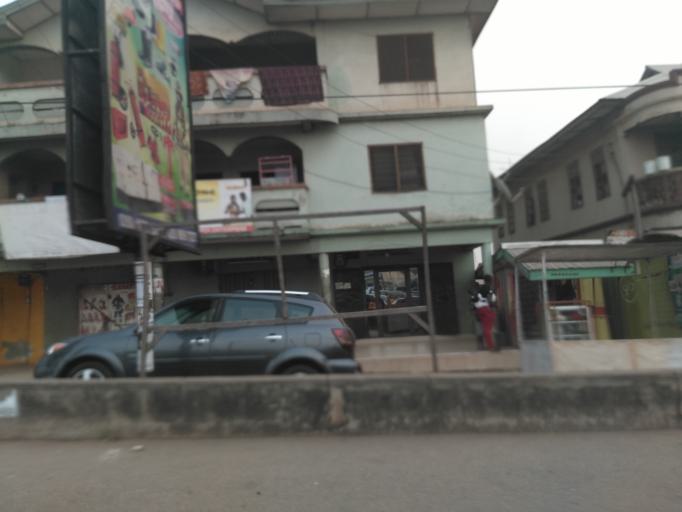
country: GH
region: Ashanti
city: Kumasi
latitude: 6.6891
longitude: -1.6004
